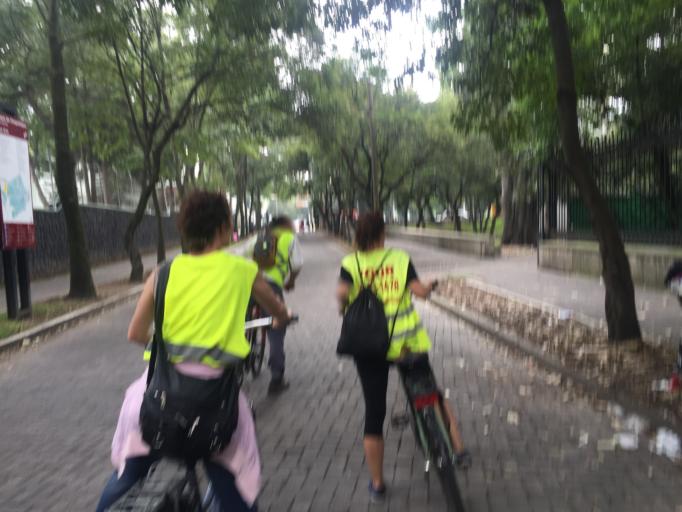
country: MX
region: Mexico City
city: Polanco
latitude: 19.4212
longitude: -99.1915
